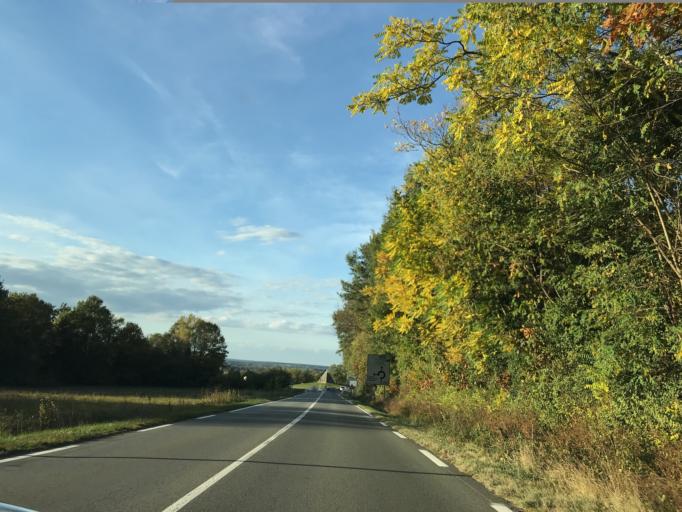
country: FR
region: Auvergne
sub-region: Departement du Puy-de-Dome
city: Paslieres
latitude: 45.9451
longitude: 3.4842
